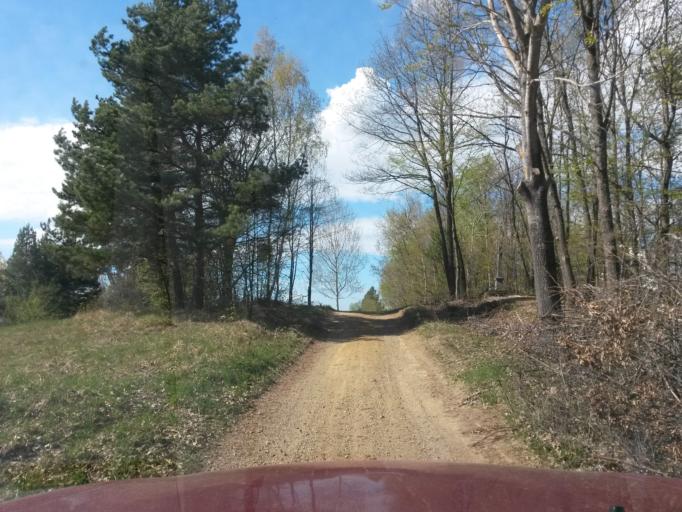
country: SK
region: Presovsky
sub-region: Okres Presov
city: Presov
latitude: 48.9375
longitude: 21.1223
